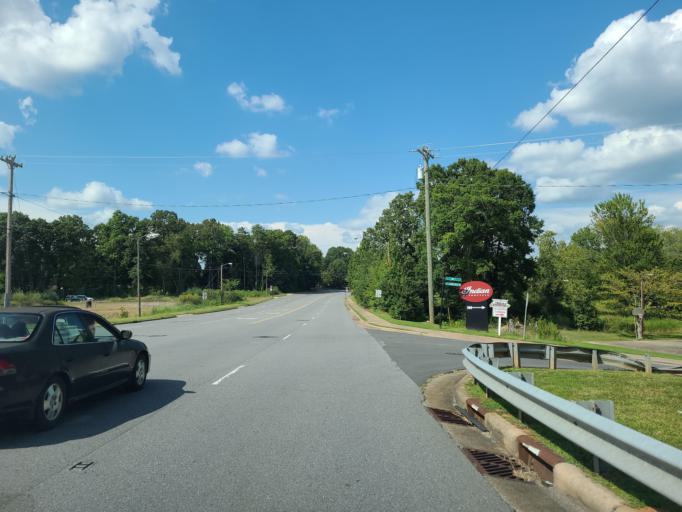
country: US
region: North Carolina
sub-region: Gaston County
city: Lowell
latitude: 35.2623
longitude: -81.1044
